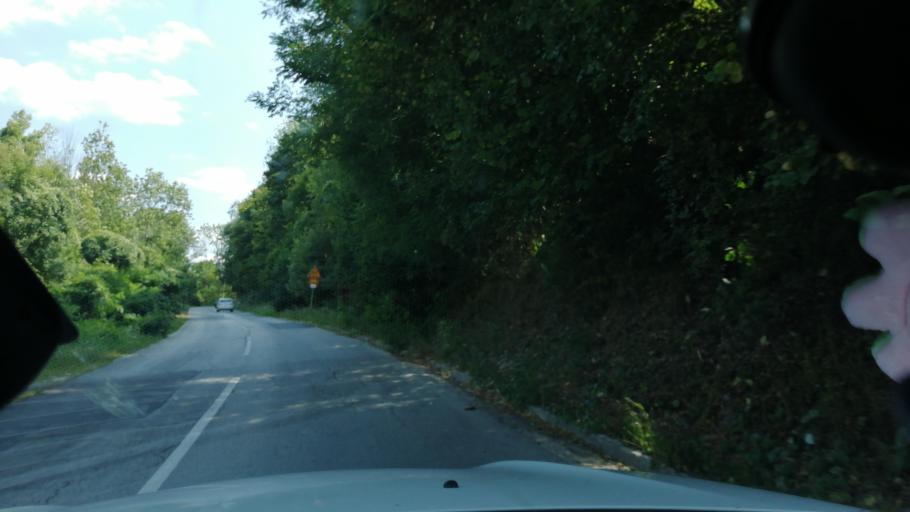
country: RS
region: Central Serbia
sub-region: Moravicki Okrug
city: Ivanjica
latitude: 43.6731
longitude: 20.2628
